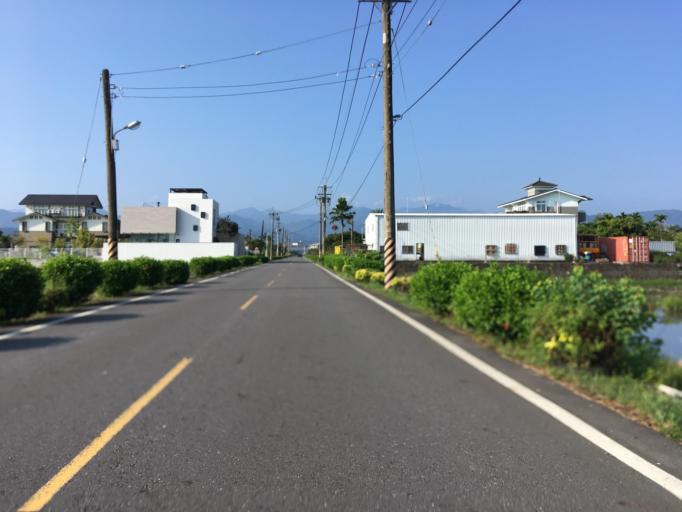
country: TW
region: Taiwan
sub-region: Yilan
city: Yilan
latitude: 24.6782
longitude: 121.7345
